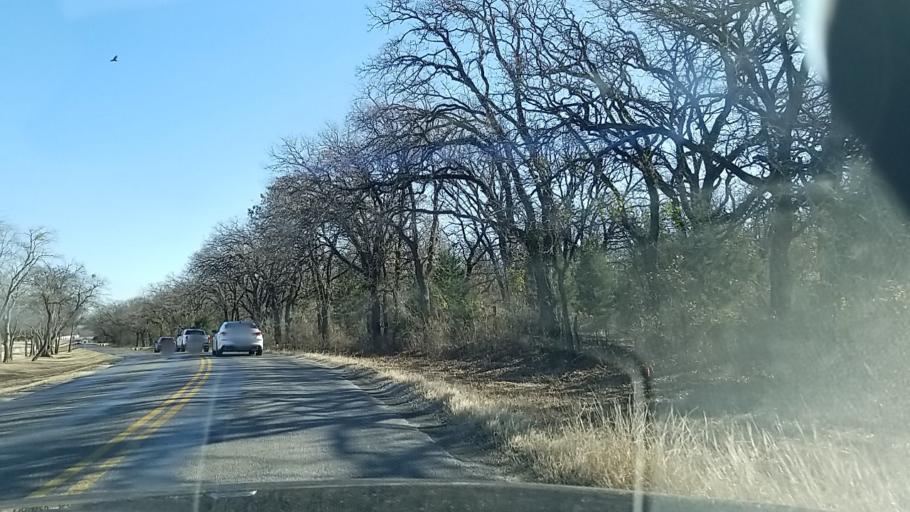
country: US
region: Texas
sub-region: Denton County
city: Argyle
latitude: 33.1289
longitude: -97.1925
